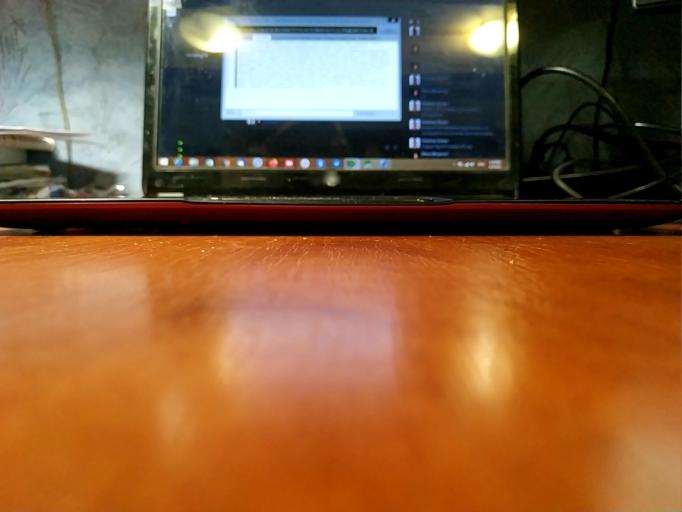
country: RU
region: Tverskaya
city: Sandovo
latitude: 58.5093
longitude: 36.3932
